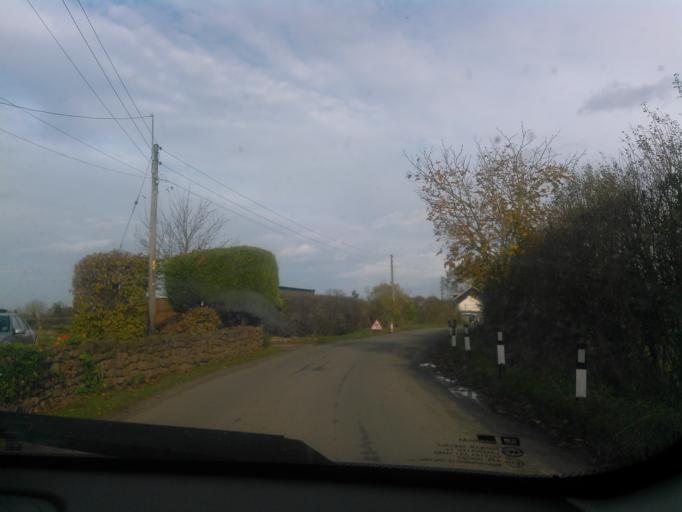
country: GB
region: England
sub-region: Shropshire
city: Wem
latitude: 52.8510
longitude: -2.7026
